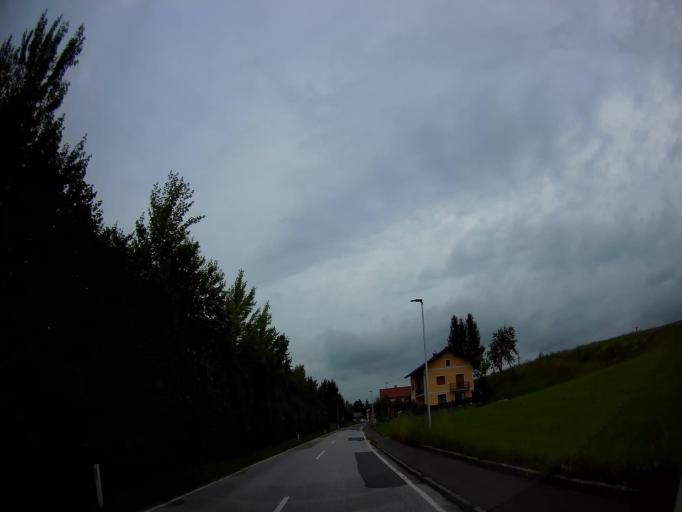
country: AT
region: Salzburg
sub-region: Politischer Bezirk Salzburg-Umgebung
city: Mattsee
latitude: 48.0804
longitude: 13.1460
